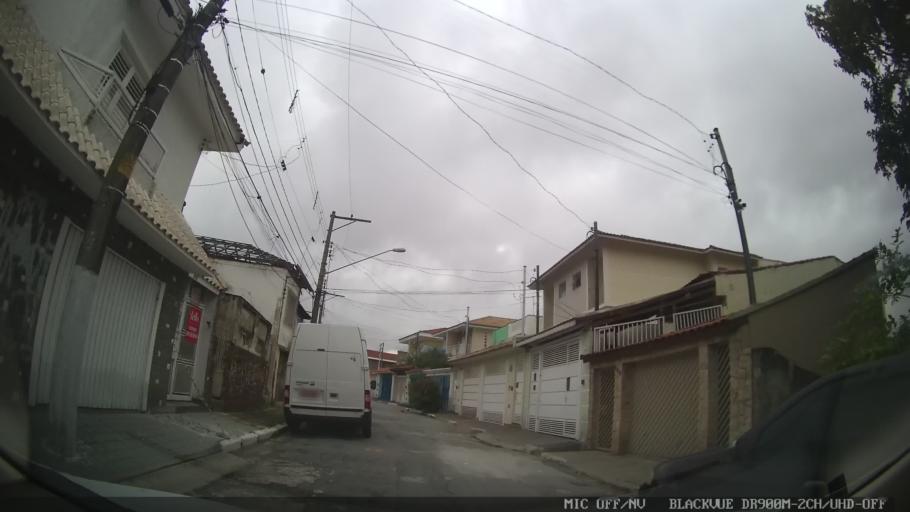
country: BR
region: Sao Paulo
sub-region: Sao Paulo
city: Sao Paulo
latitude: -23.4975
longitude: -46.6049
